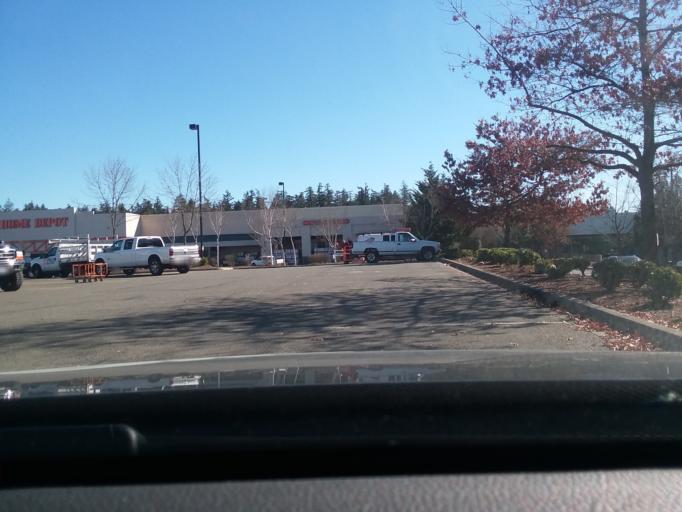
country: US
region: Washington
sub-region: Pierce County
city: Puyallup
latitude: 47.1586
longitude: -122.2912
